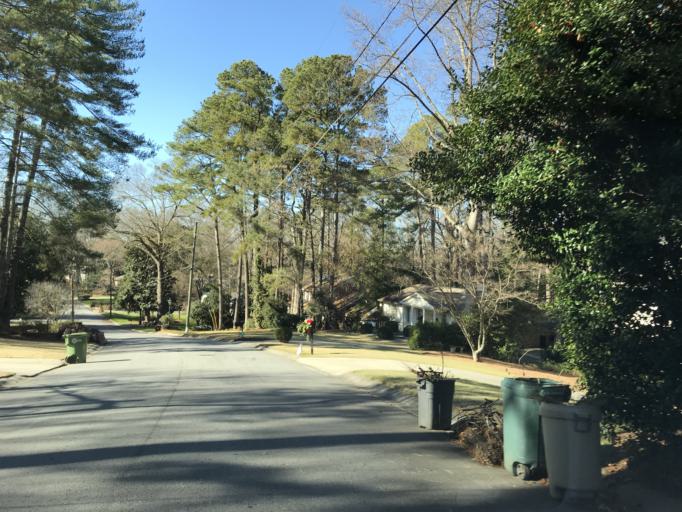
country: US
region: Georgia
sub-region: DeKalb County
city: North Atlanta
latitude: 33.8812
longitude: -84.3504
